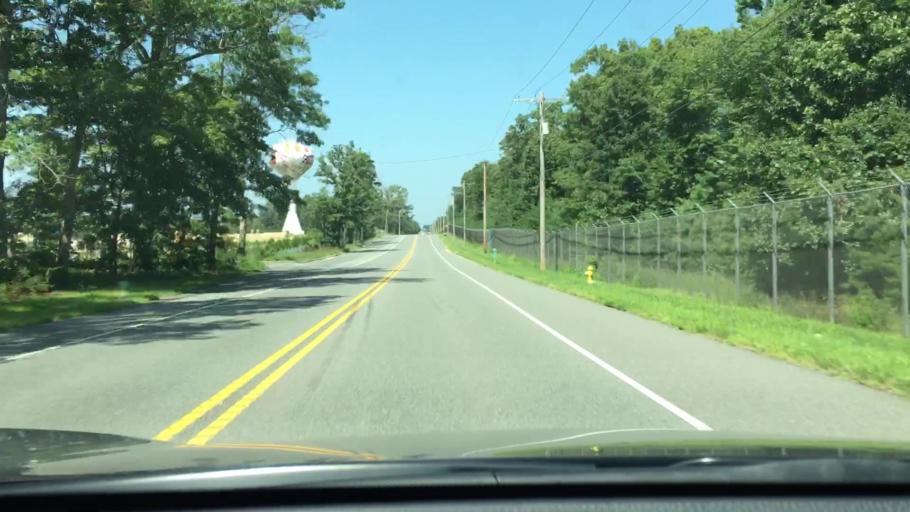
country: US
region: New Jersey
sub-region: Cumberland County
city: Laurel Lake
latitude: 39.3583
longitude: -75.0704
